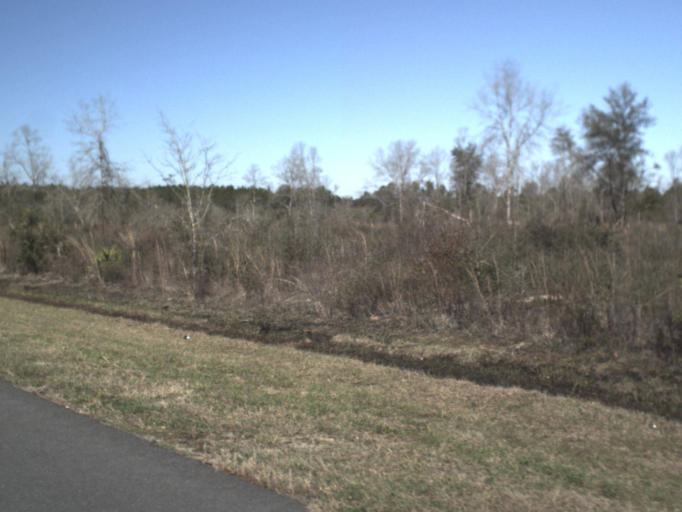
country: US
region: Florida
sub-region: Bay County
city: Callaway
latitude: 30.1495
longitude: -85.4687
